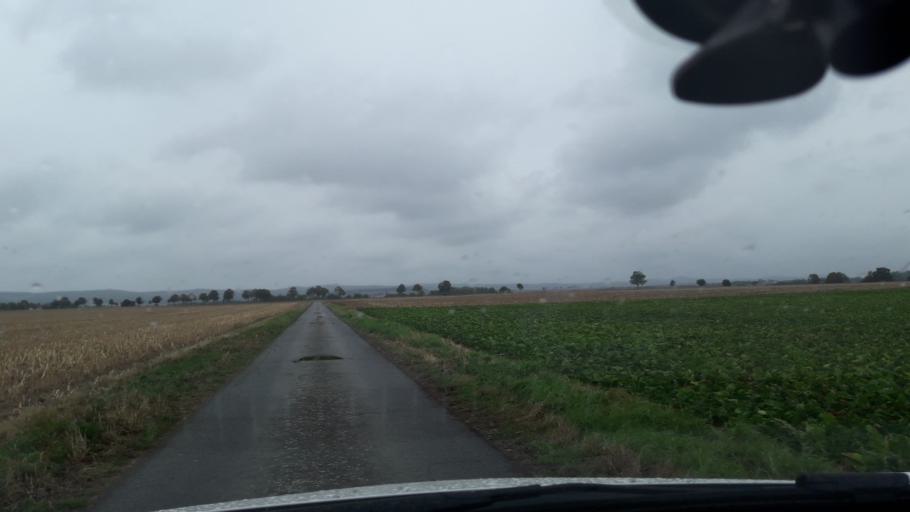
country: DE
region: Lower Saxony
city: Schladen
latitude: 51.9942
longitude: 10.5375
